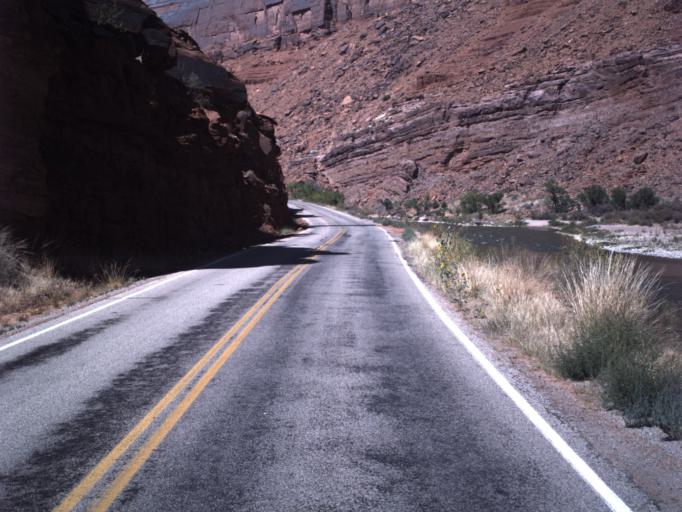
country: US
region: Utah
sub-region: Grand County
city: Moab
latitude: 38.6822
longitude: -109.4559
